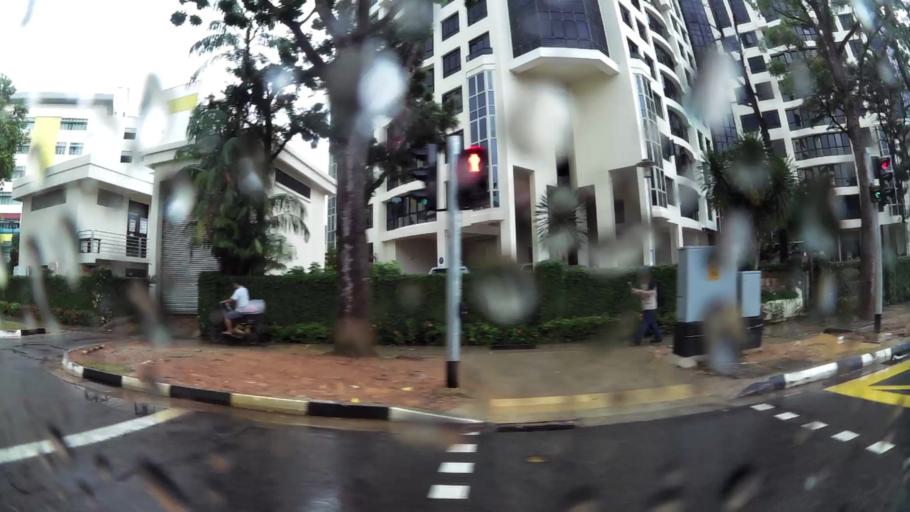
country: SG
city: Singapore
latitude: 1.3399
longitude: 103.9510
